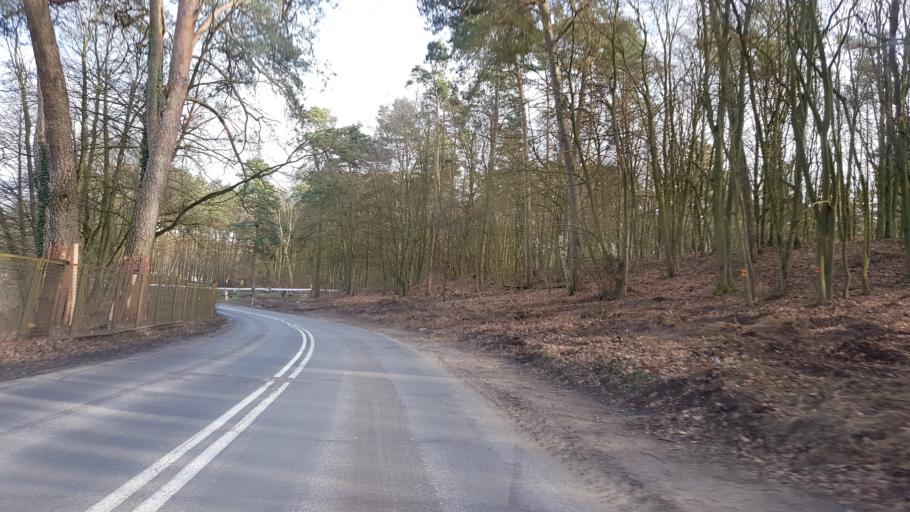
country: PL
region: West Pomeranian Voivodeship
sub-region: Szczecin
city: Szczecin
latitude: 53.4713
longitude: 14.4817
